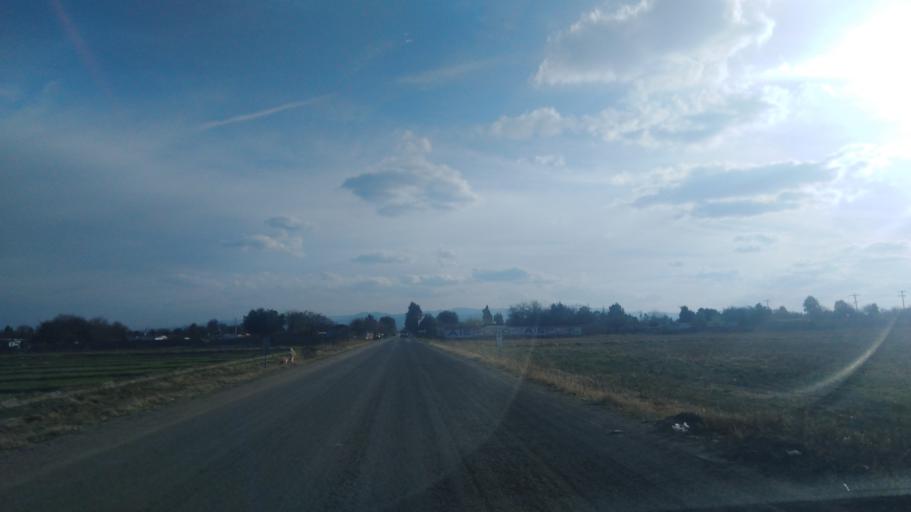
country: MX
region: Durango
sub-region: Durango
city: Jose Refugio Salcido
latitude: 23.9973
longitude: -104.4778
